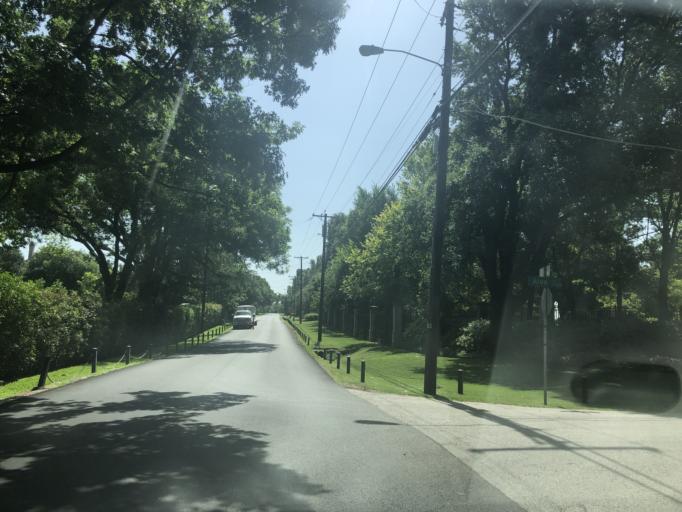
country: US
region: Texas
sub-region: Dallas County
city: University Park
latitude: 32.8740
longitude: -96.8159
